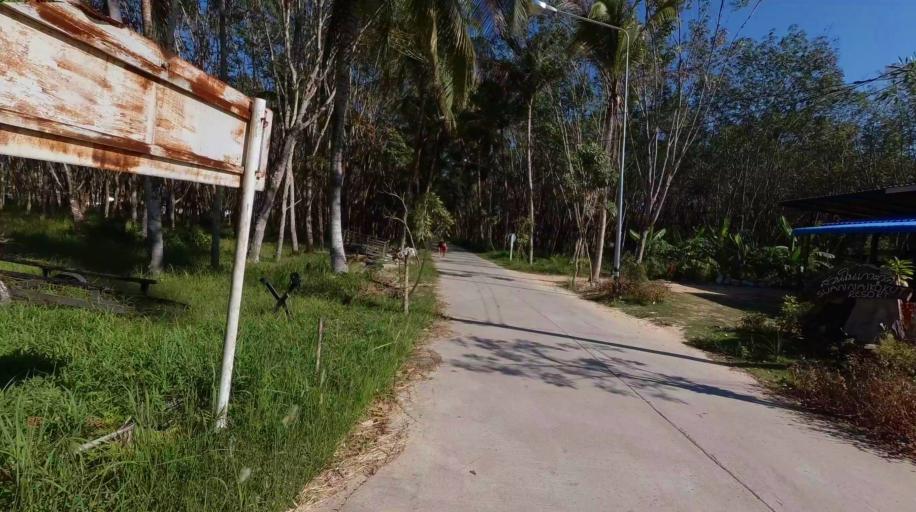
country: TH
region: Trat
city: Ko Kut
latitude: 11.6203
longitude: 102.5502
